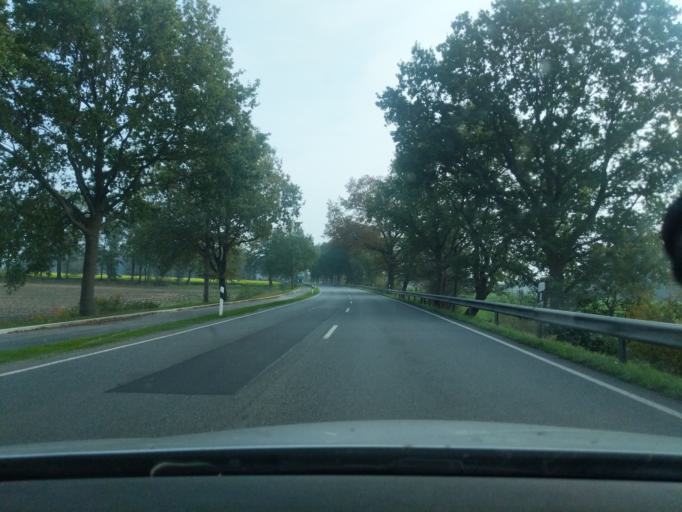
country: DE
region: Lower Saxony
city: Himmelpforten
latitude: 53.5987
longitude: 9.3237
